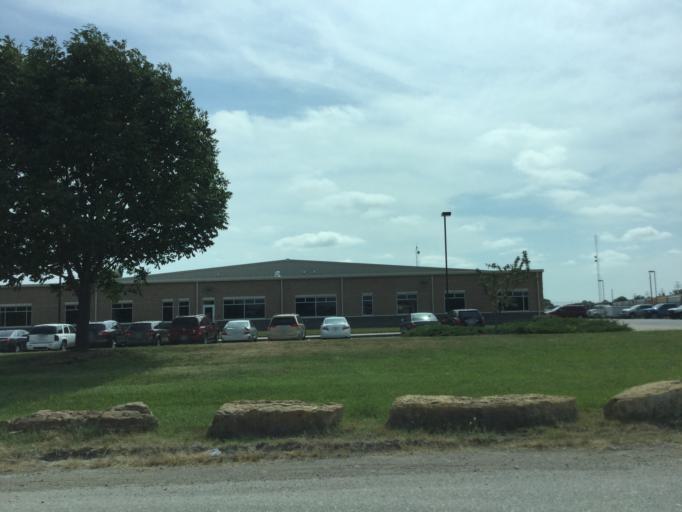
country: US
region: Kansas
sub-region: Shawnee County
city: Topeka
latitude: 39.0845
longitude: -95.7251
